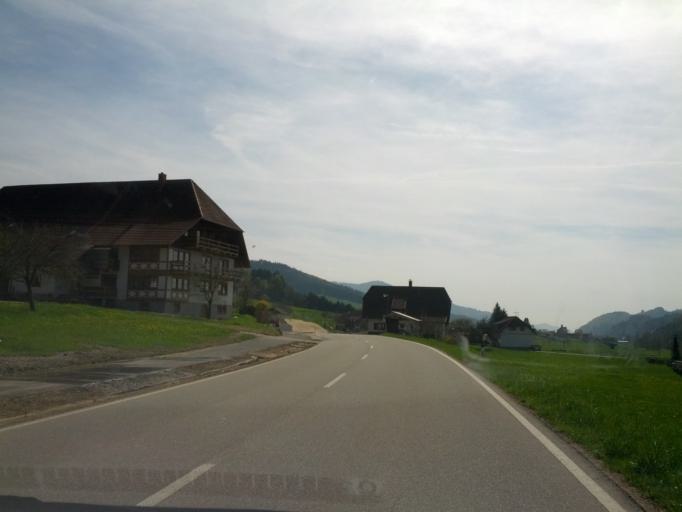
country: DE
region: Baden-Wuerttemberg
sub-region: Freiburg Region
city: Elzach
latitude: 48.1921
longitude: 8.0979
